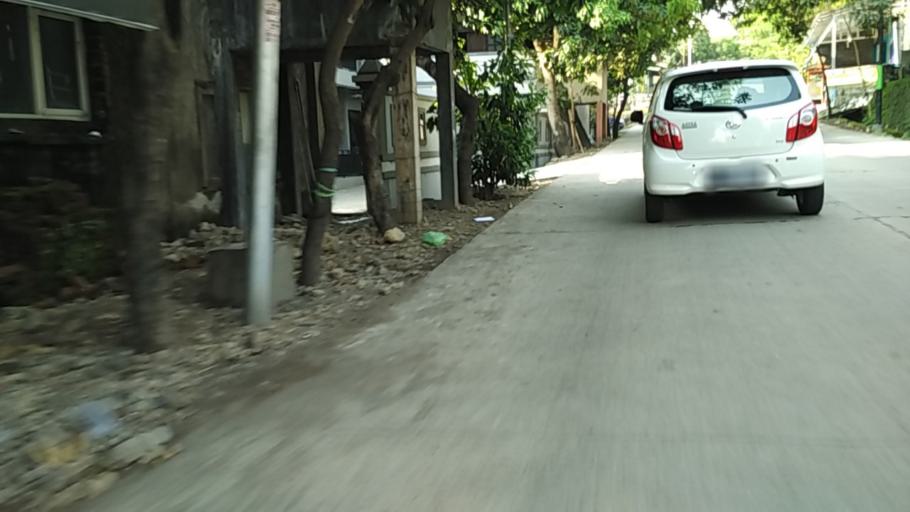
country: ID
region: Central Java
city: Mranggen
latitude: -7.0563
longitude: 110.4637
